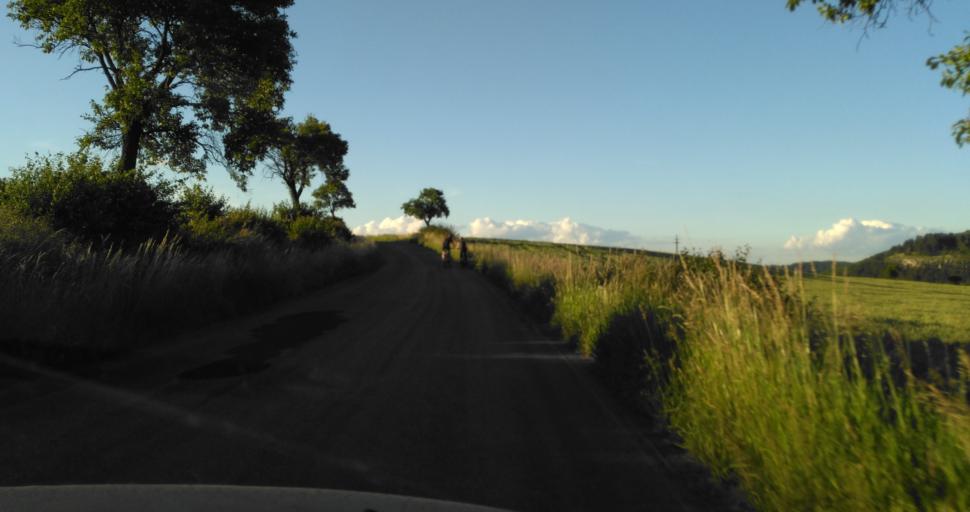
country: CZ
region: Central Bohemia
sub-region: Okres Beroun
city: Kraluv Dvur
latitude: 49.9101
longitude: 14.0334
